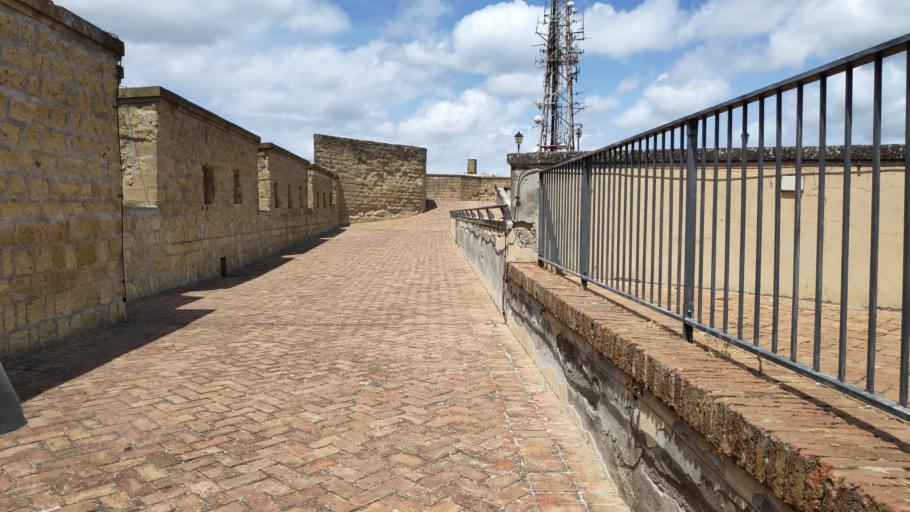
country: IT
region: Campania
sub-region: Provincia di Napoli
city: Napoli
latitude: 40.8437
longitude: 14.2386
